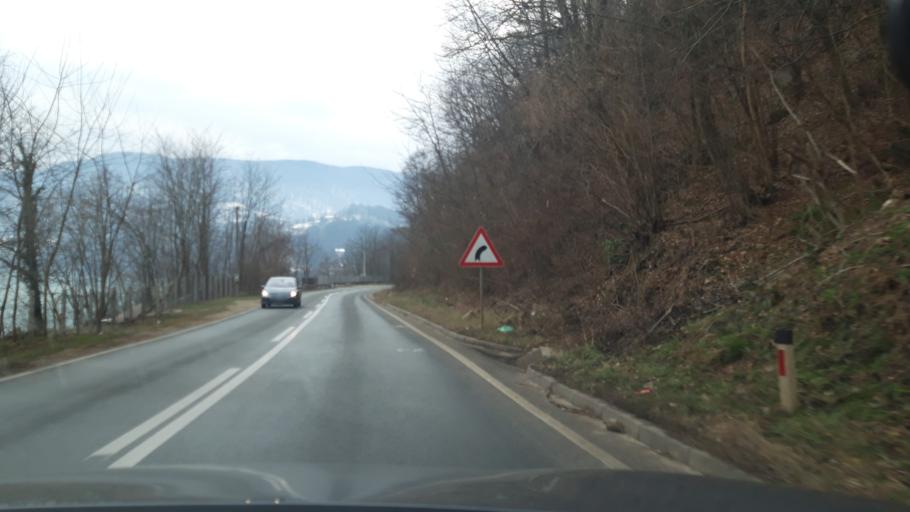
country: RS
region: Central Serbia
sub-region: Macvanski Okrug
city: Mali Zvornik
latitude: 44.3342
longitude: 19.1322
